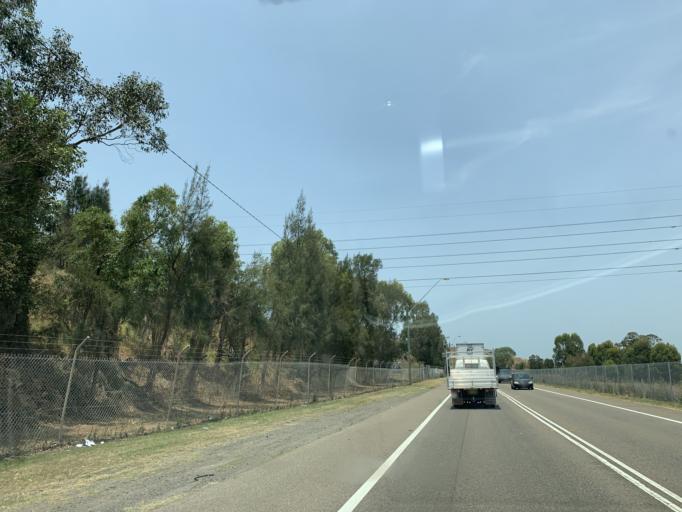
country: AU
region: New South Wales
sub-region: Blacktown
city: Doonside
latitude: -33.8043
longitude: 150.8644
